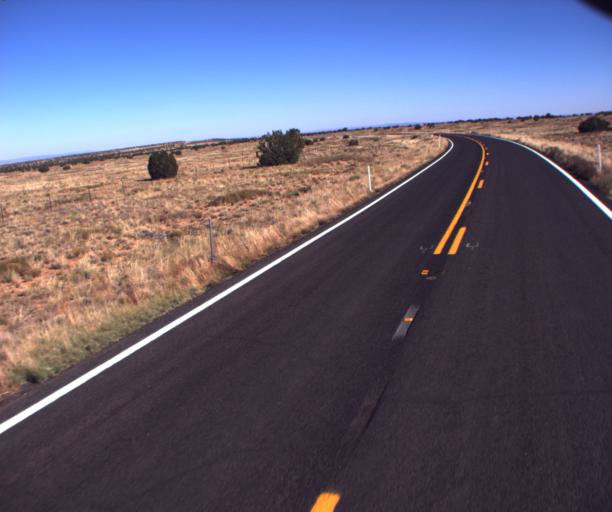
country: US
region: Arizona
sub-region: Coconino County
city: Tuba City
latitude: 35.9144
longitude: -110.8627
